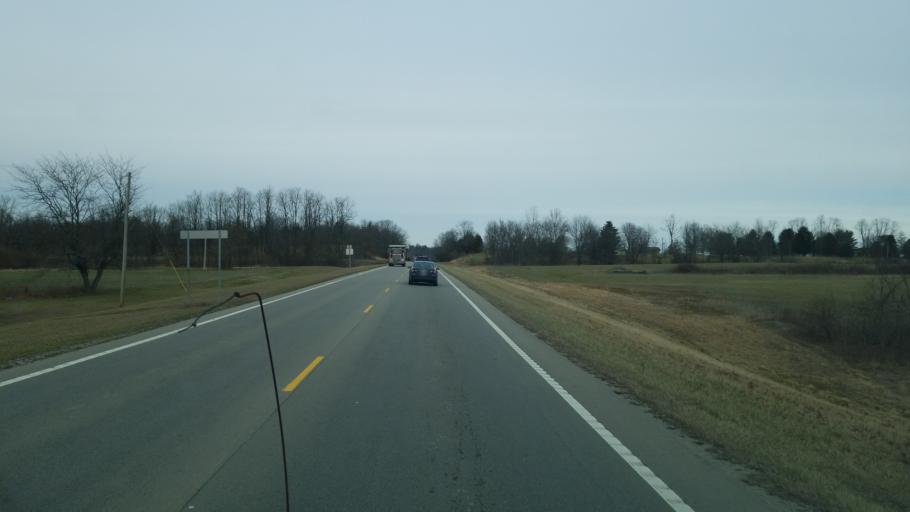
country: US
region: Ohio
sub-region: Highland County
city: Hillsboro
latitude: 39.1174
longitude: -83.6746
